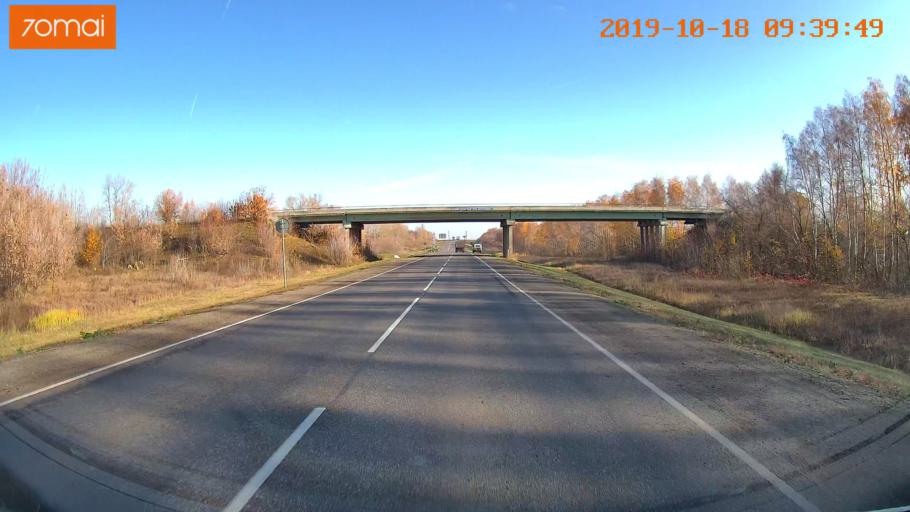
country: RU
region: Tula
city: Yefremov
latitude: 53.2574
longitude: 38.1400
